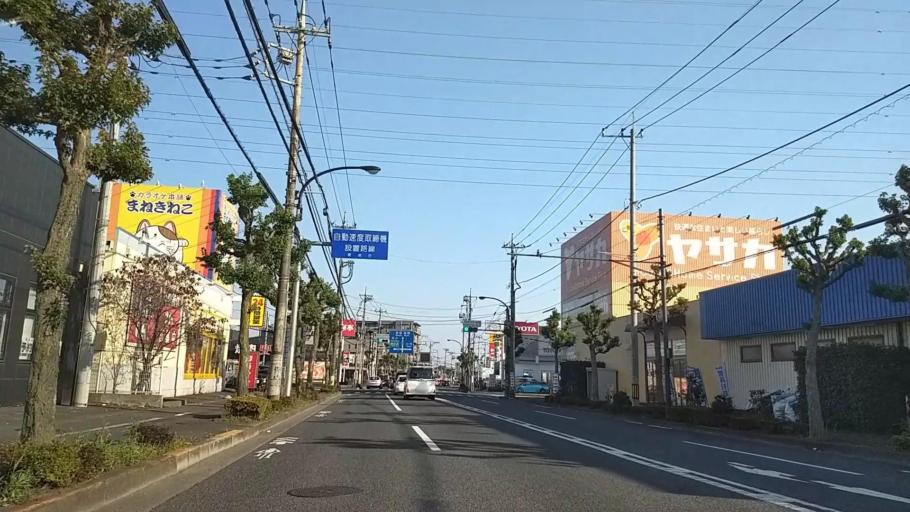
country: JP
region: Tokyo
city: Fussa
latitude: 35.7863
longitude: 139.3075
